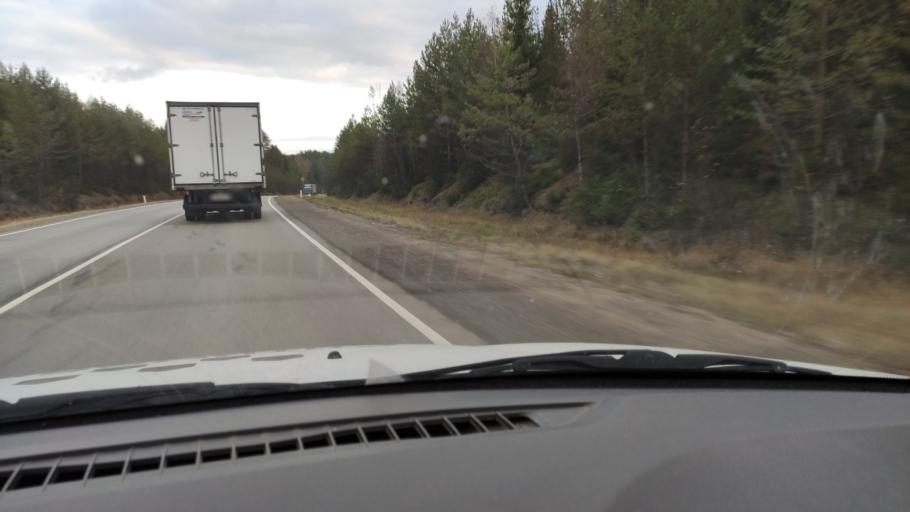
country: RU
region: Kirov
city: Chernaya Kholunitsa
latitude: 58.8508
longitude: 51.7402
